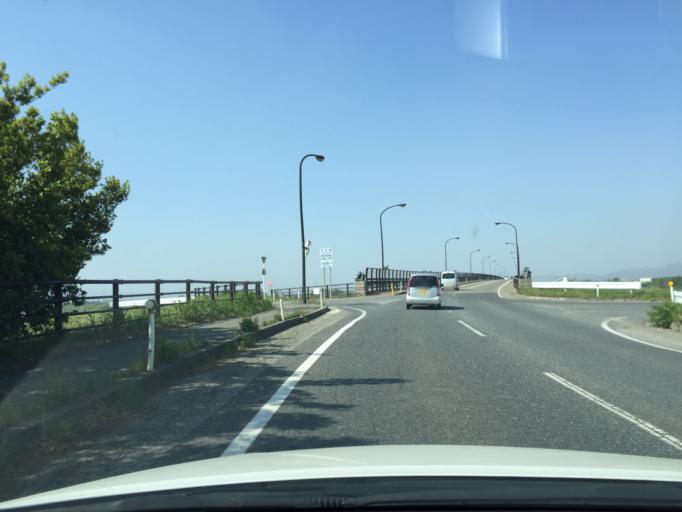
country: JP
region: Niigata
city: Gosen
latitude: 37.7542
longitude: 139.2281
